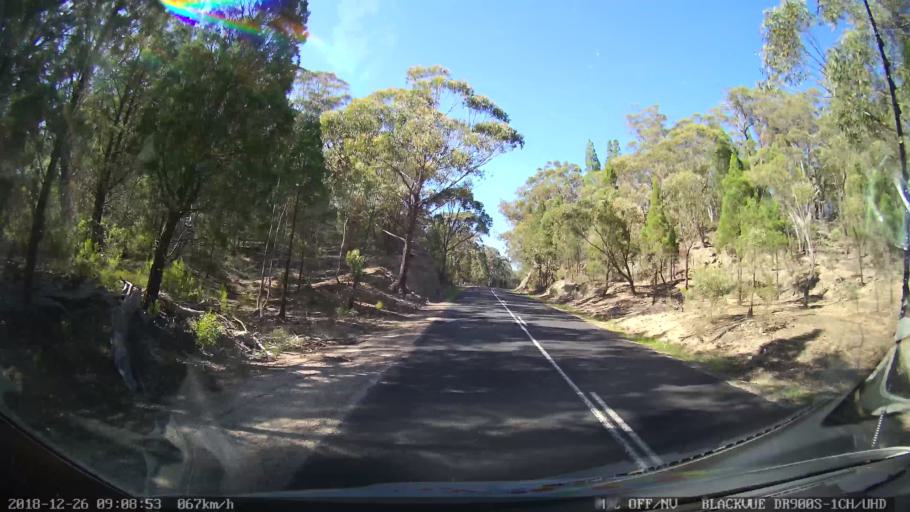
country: AU
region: New South Wales
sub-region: Mid-Western Regional
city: Kandos
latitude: -32.7195
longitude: 149.9997
